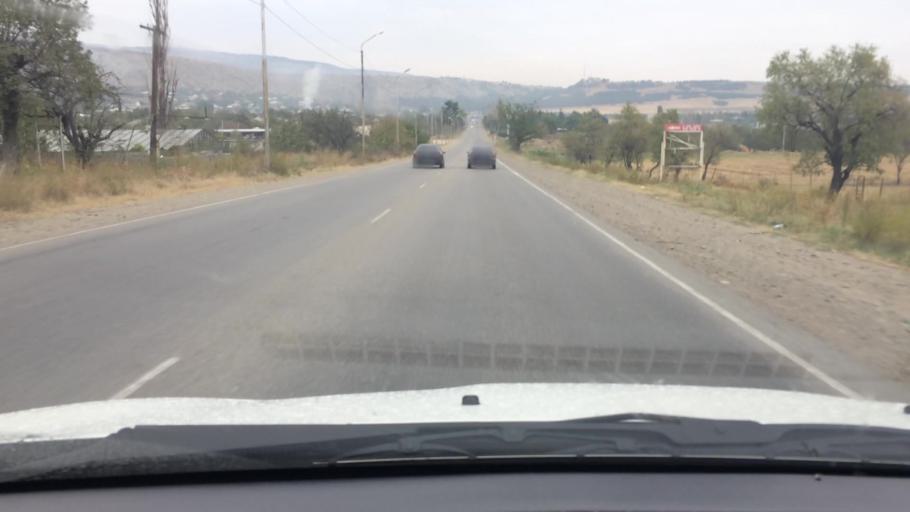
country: GE
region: T'bilisi
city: Tbilisi
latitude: 41.6029
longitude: 44.7813
